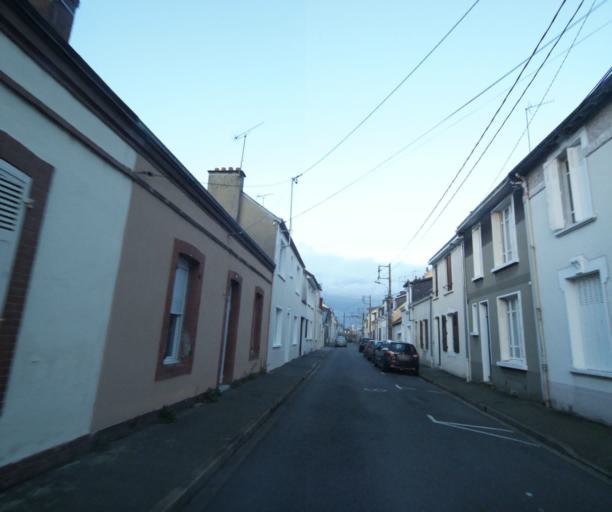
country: FR
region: Pays de la Loire
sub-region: Departement de la Sarthe
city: Le Mans
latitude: 47.9903
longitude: 0.1997
